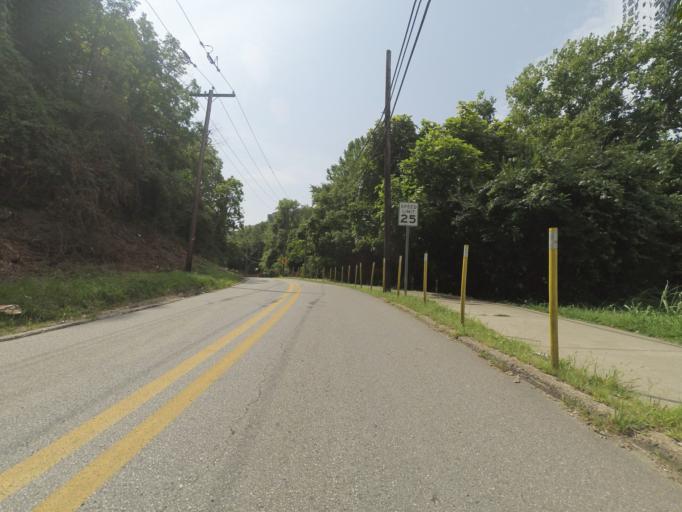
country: US
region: West Virginia
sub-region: Cabell County
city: Huntington
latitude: 38.4032
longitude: -82.4781
